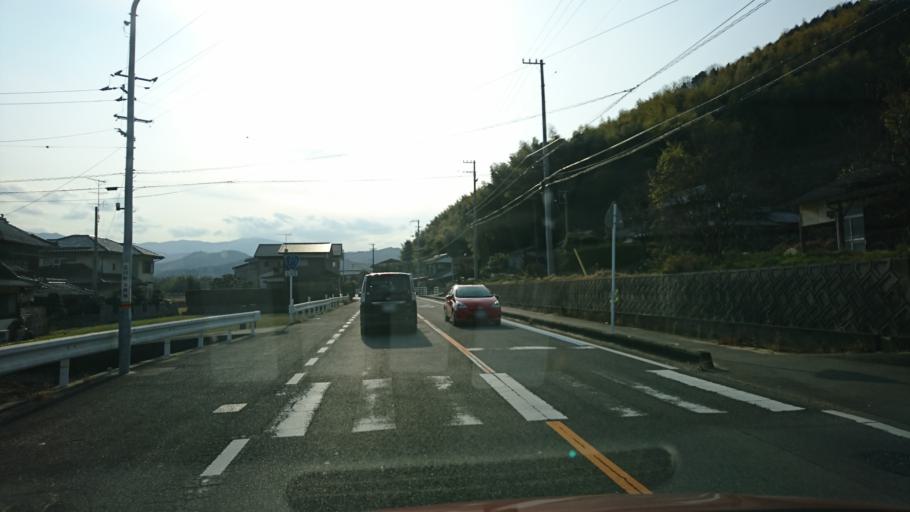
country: JP
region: Ehime
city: Hojo
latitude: 34.0260
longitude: 132.9474
